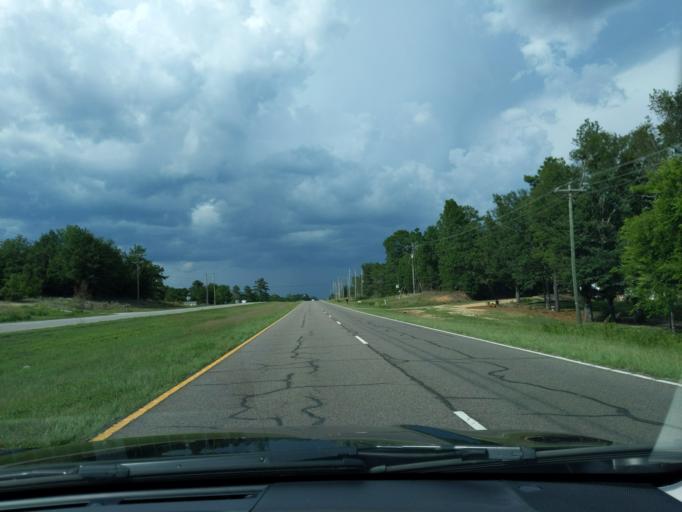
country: US
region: South Carolina
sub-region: Edgefield County
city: Murphys Estates
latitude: 33.6308
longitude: -81.9162
